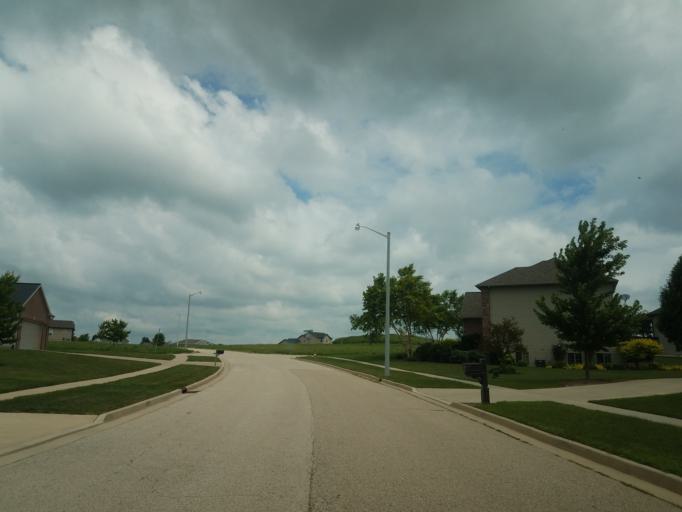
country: US
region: Illinois
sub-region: McLean County
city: Bloomington
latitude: 40.4444
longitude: -89.0381
